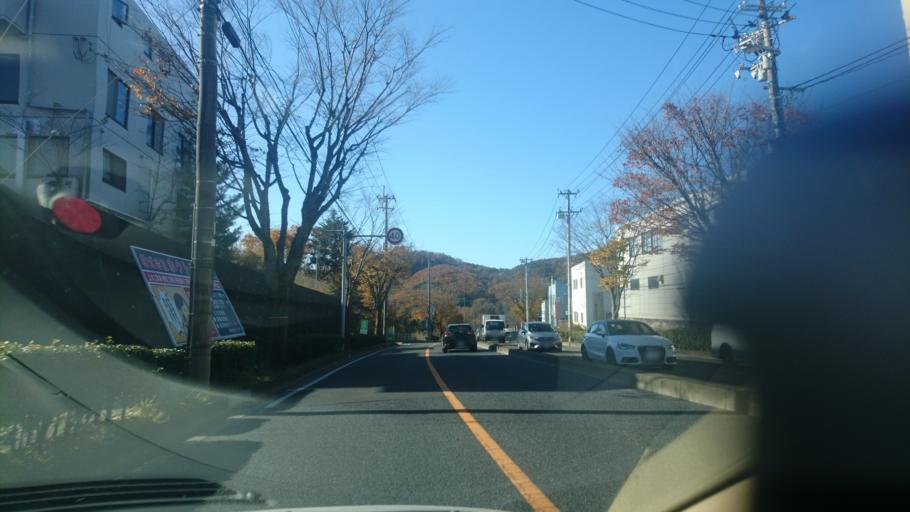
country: JP
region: Miyagi
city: Sendai
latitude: 38.2838
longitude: 140.8152
